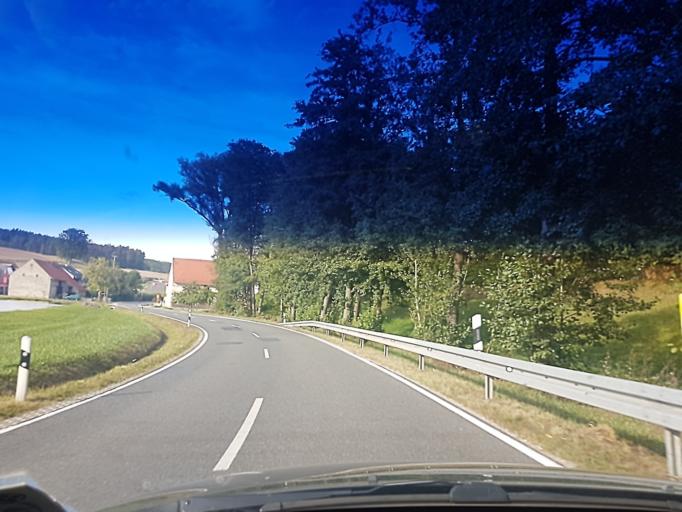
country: DE
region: Bavaria
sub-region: Upper Franconia
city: Burgwindheim
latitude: 49.8078
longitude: 10.5846
